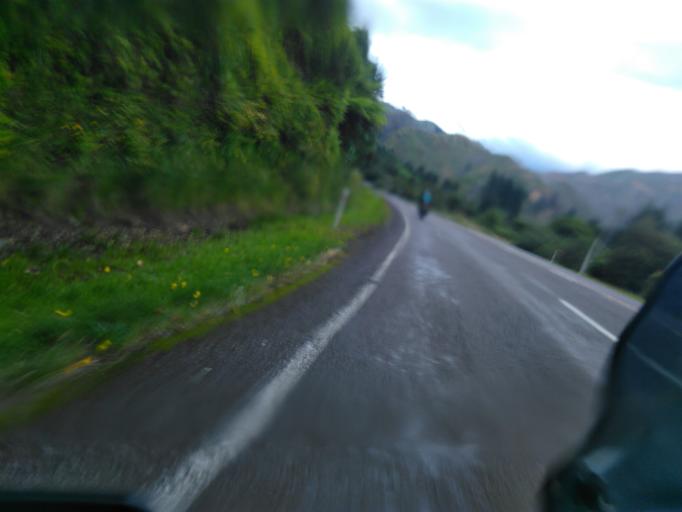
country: NZ
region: Bay of Plenty
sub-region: Opotiki District
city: Opotiki
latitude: -38.2568
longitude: 177.2985
